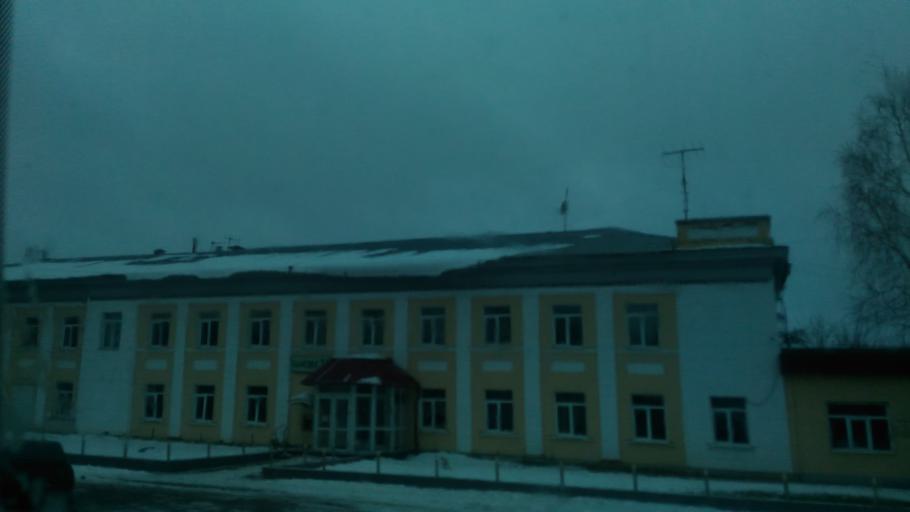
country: RU
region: Tula
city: Bolokhovo
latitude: 54.0636
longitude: 37.8010
